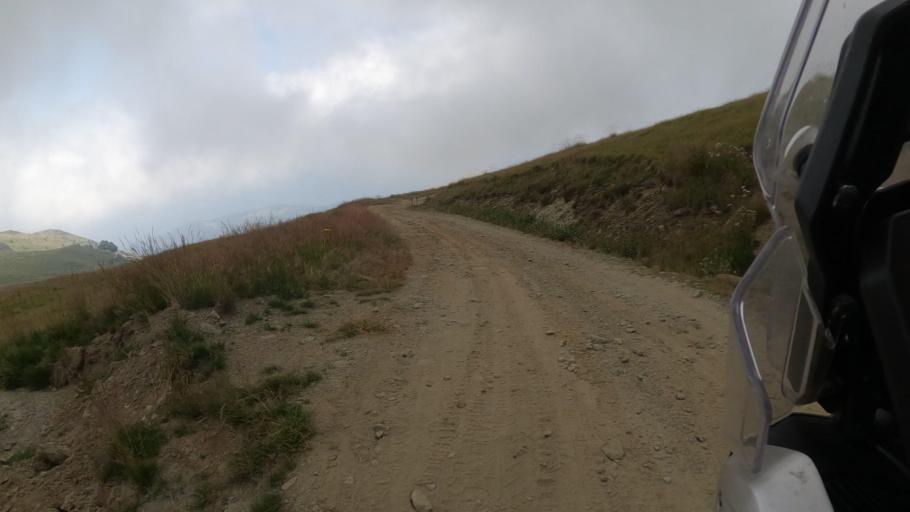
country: IT
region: Piedmont
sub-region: Provincia di Torino
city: Lemie
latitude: 45.1720
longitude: 7.2801
